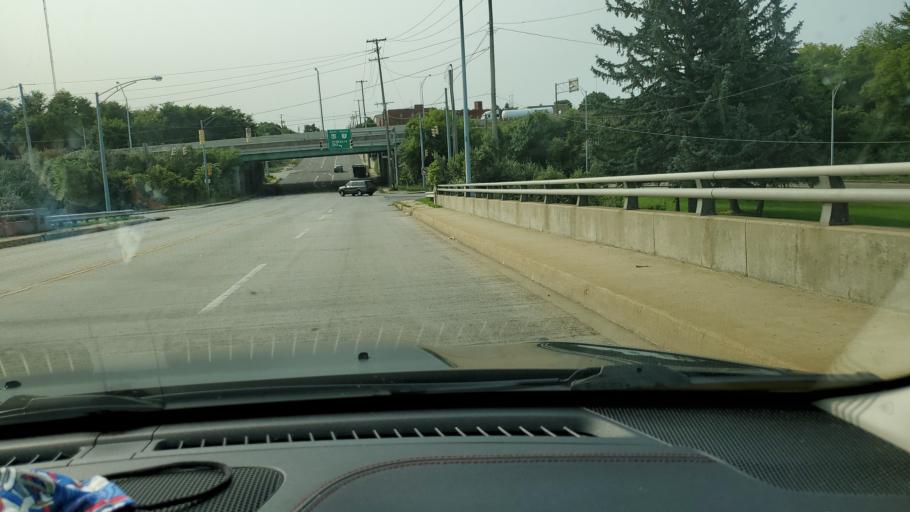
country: US
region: Ohio
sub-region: Mahoning County
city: Youngstown
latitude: 41.0937
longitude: -80.6462
